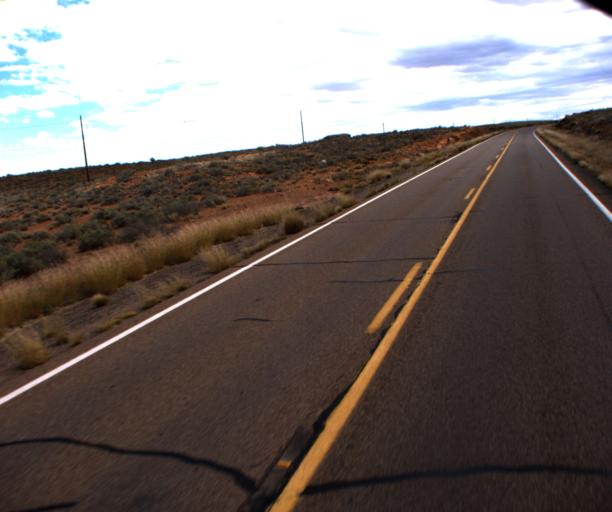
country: US
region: Arizona
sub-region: Navajo County
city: Holbrook
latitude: 34.8557
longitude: -110.1511
